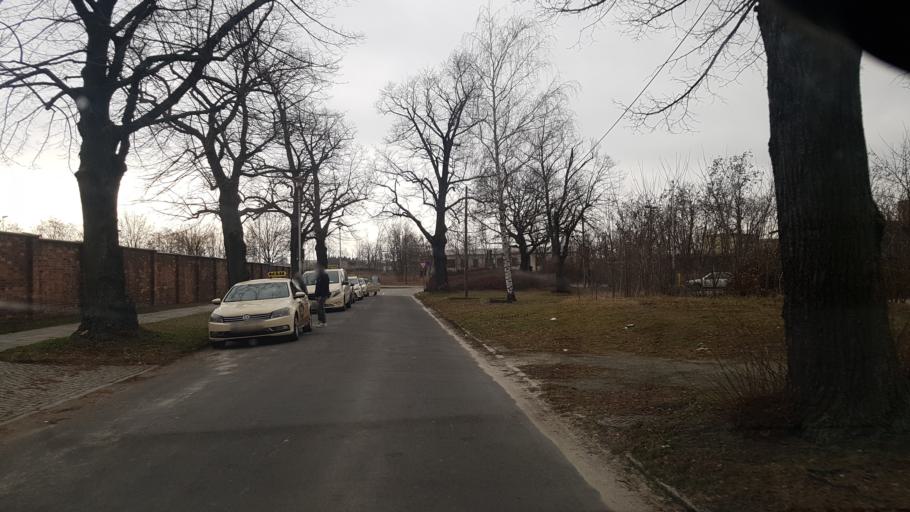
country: DE
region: Brandenburg
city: Cottbus
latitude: 51.7555
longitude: 14.3183
